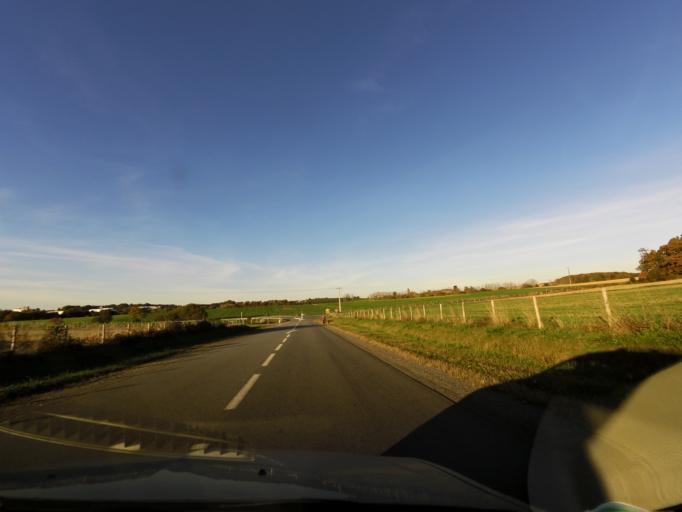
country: FR
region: Brittany
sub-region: Departement d'Ille-et-Vilaine
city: Crevin
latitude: 47.9138
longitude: -1.6733
